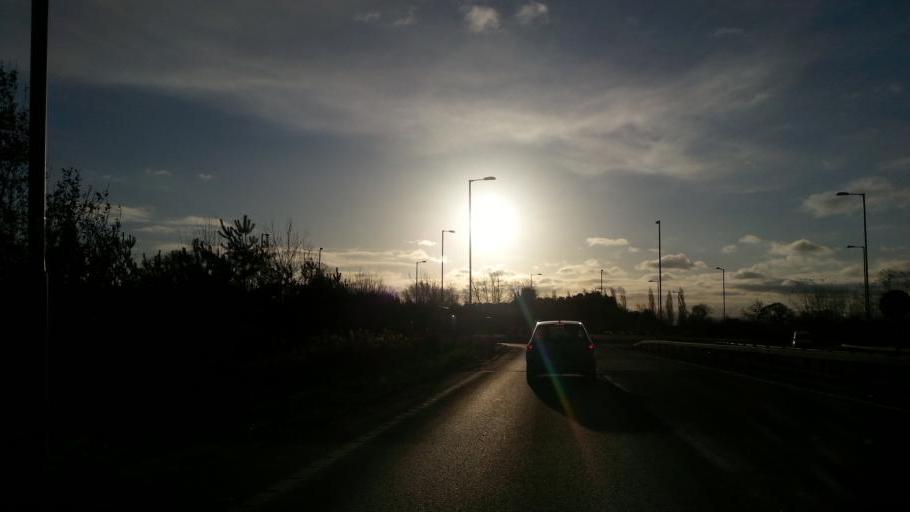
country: GB
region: England
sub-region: Peterborough
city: Thorney
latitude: 52.6214
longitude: -0.1201
